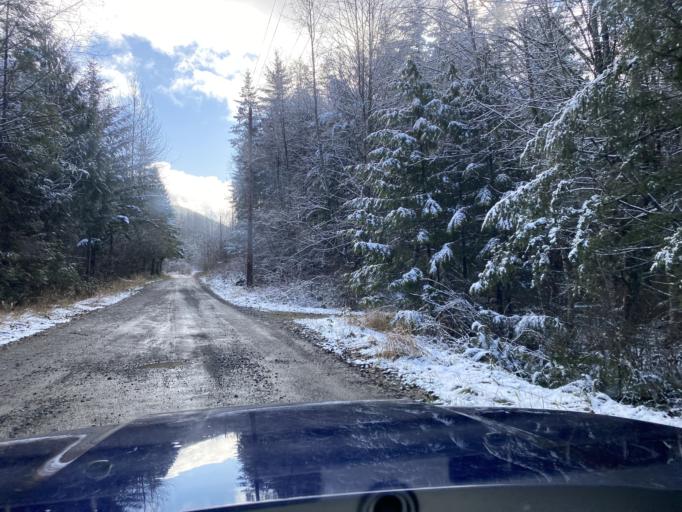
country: US
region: Washington
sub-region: King County
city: Snoqualmie
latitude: 47.4975
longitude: -121.8751
